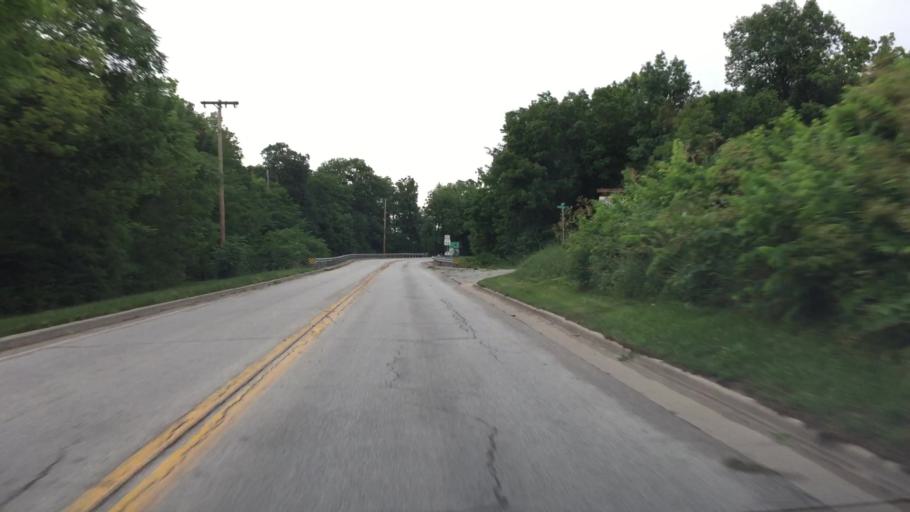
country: US
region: Illinois
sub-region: Hancock County
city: Hamilton
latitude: 40.3948
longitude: -91.3539
